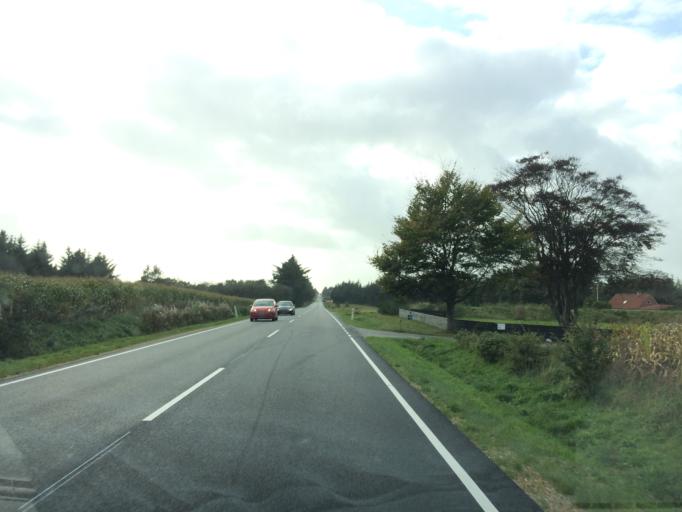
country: DK
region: Central Jutland
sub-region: Holstebro Kommune
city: Ulfborg
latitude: 56.3075
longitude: 8.4021
